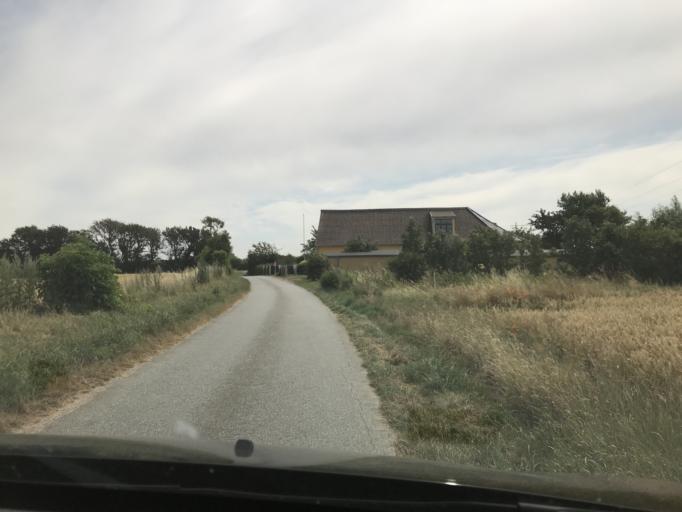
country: DK
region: South Denmark
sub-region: AEro Kommune
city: AEroskobing
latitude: 54.9191
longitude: 10.2509
